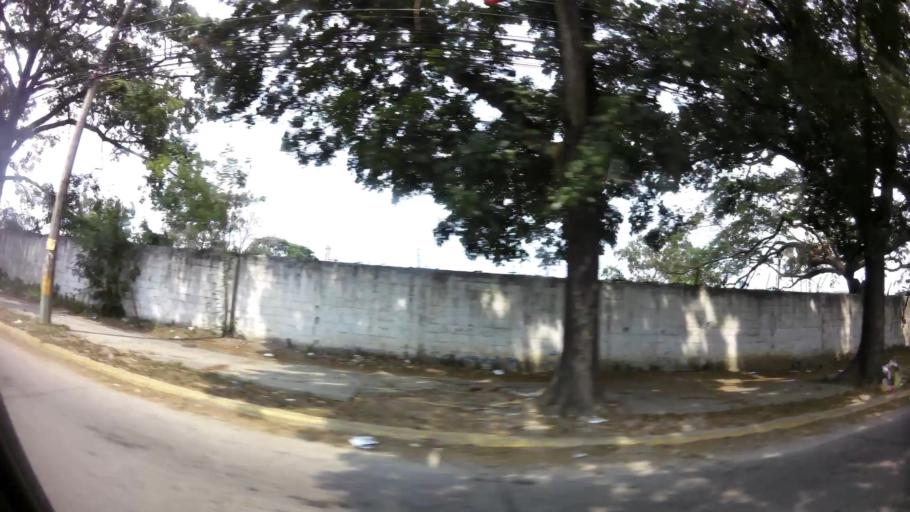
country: HN
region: Cortes
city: San Pedro Sula
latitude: 15.5145
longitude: -88.0126
